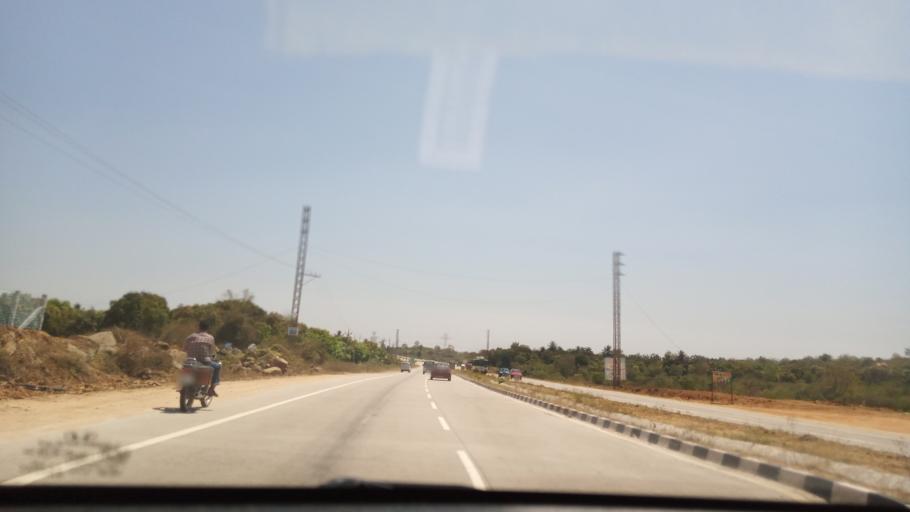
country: IN
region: Andhra Pradesh
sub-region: Chittoor
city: Chittoor
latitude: 13.2001
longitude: 78.9704
